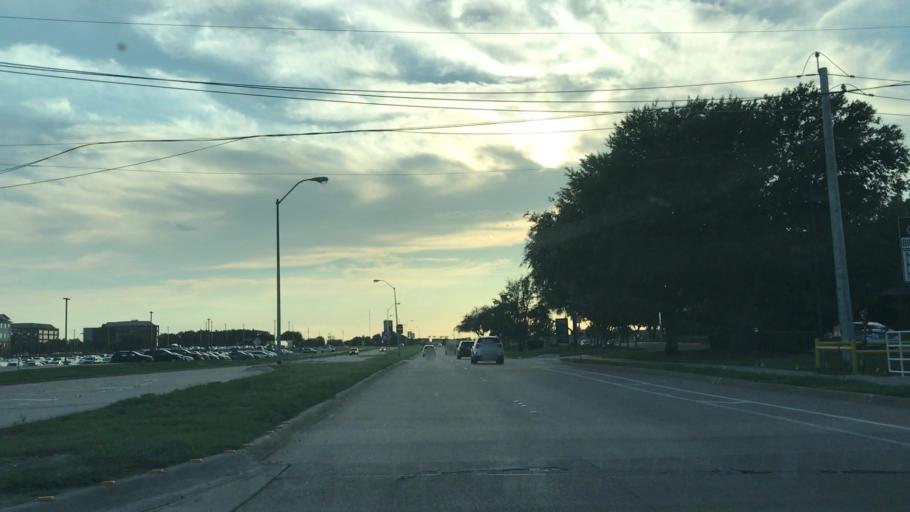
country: US
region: Texas
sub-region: Dallas County
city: Richardson
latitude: 32.9931
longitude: -96.7511
